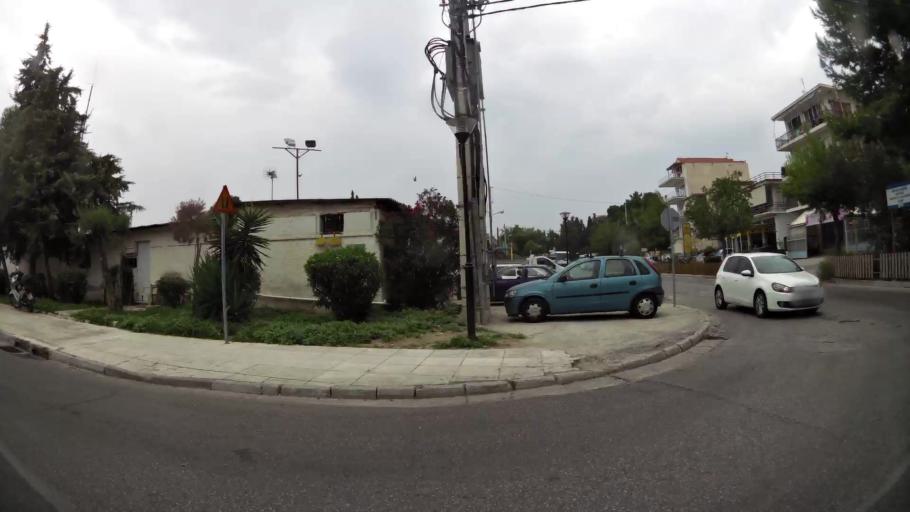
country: GR
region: Attica
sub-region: Nomarchia Athinas
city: Palaio Faliro
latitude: 37.9294
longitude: 23.7150
